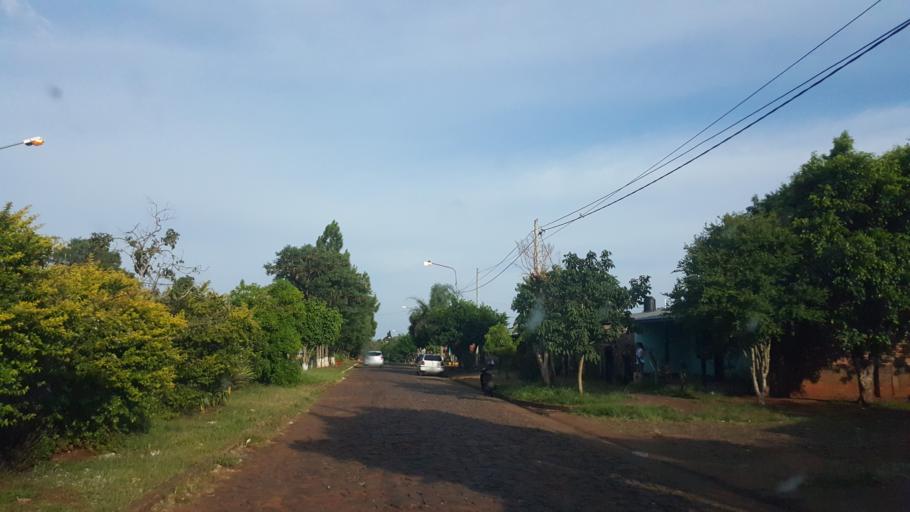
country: AR
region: Misiones
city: Garupa
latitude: -27.4358
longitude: -55.8746
